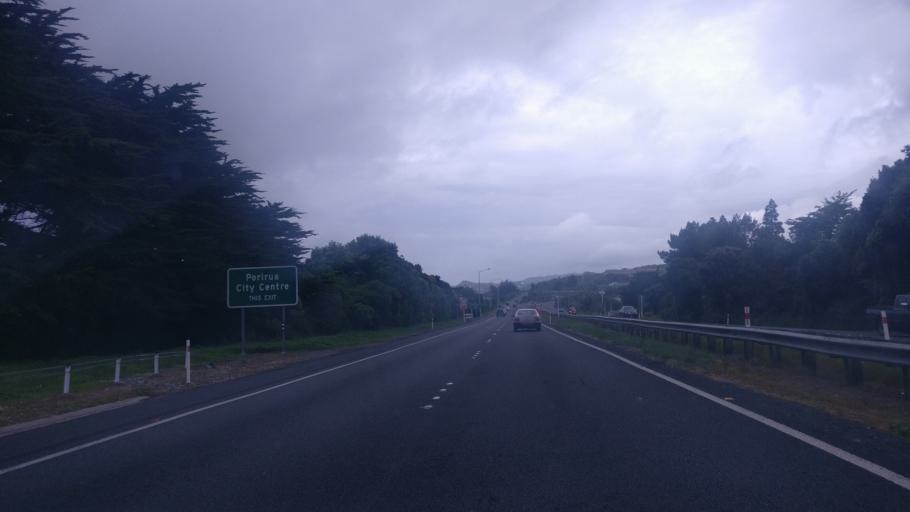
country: NZ
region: Wellington
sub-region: Porirua City
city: Porirua
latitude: -41.1454
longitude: 174.8443
